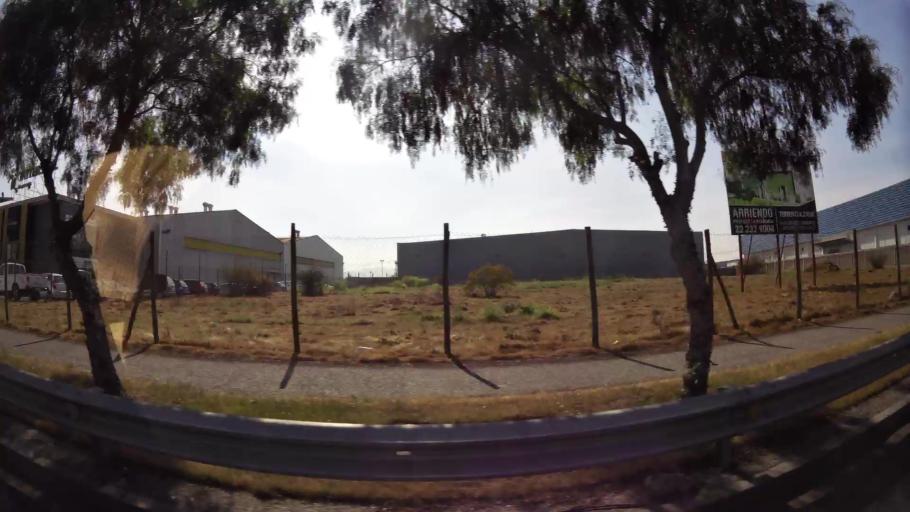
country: CL
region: Santiago Metropolitan
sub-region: Provincia de Santiago
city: Lo Prado
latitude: -33.4238
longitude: -70.7806
